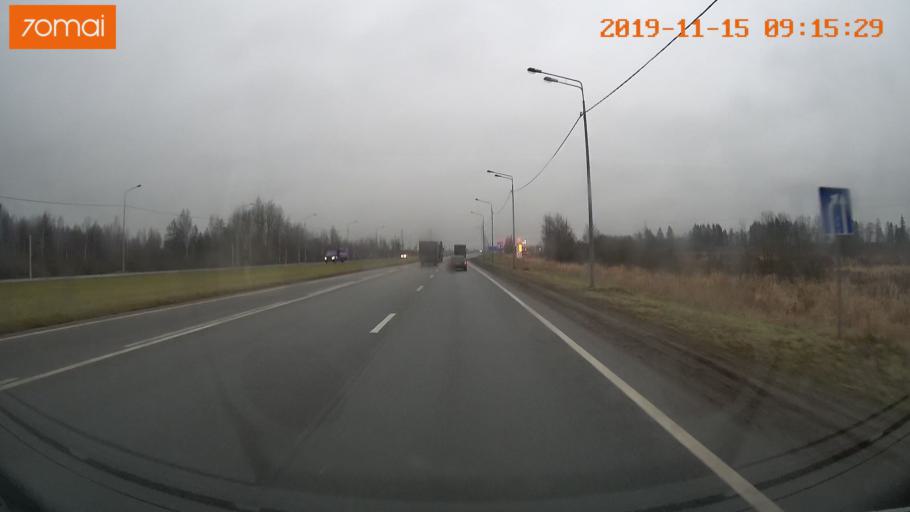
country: RU
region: Vologda
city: Tonshalovo
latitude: 59.2392
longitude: 37.9670
